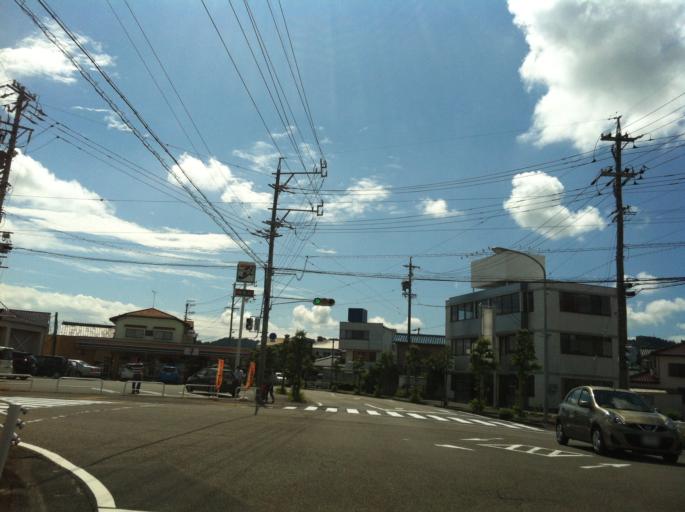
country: JP
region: Shizuoka
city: Kanaya
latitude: 34.8311
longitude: 138.1281
